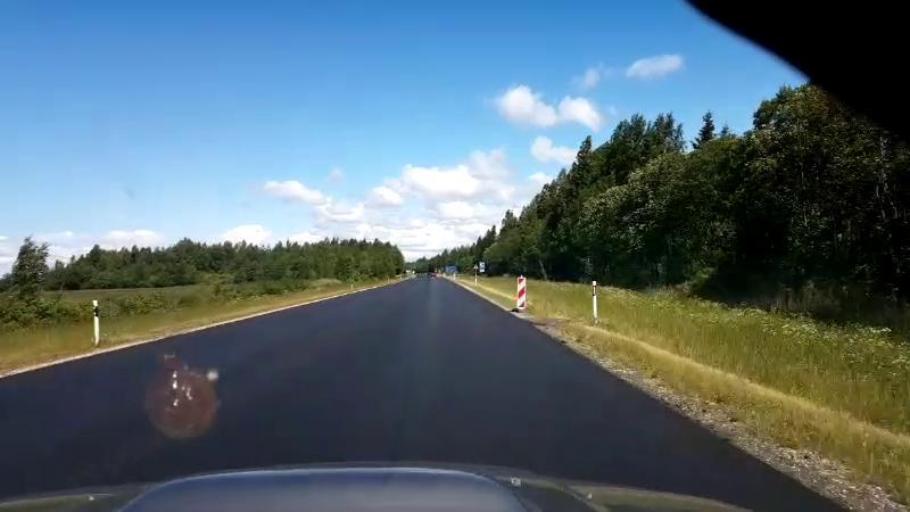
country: LV
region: Salacgrivas
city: Ainazi
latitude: 58.0102
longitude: 24.4904
